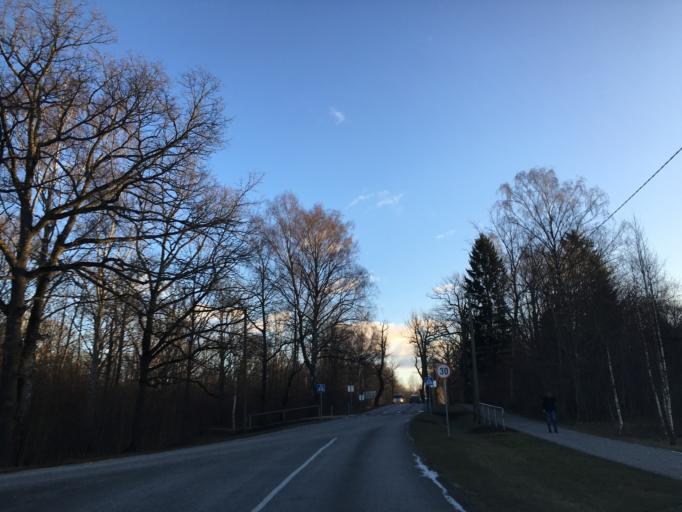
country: EE
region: Harju
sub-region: Saue linn
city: Saue
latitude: 59.3192
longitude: 24.5535
